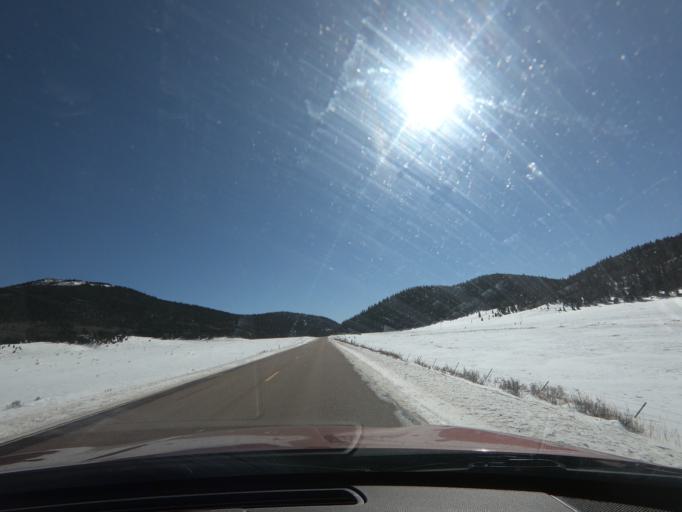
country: US
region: Colorado
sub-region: Teller County
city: Cripple Creek
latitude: 38.7604
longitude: -105.1113
